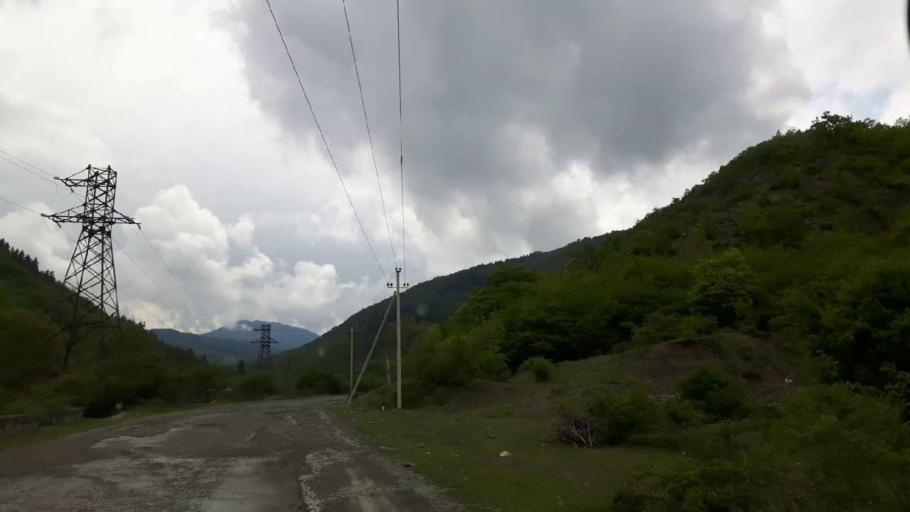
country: GE
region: Shida Kartli
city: Gori
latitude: 41.8830
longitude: 43.9970
